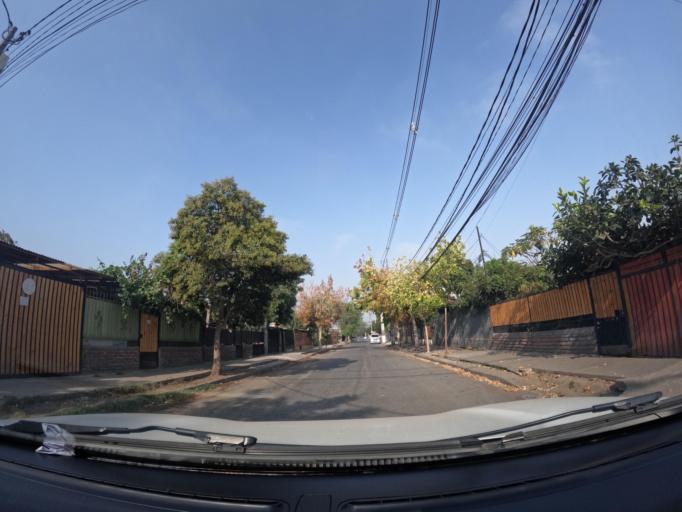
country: CL
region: Santiago Metropolitan
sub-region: Provincia de Santiago
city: Villa Presidente Frei, Nunoa, Santiago, Chile
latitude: -33.4752
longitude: -70.5696
